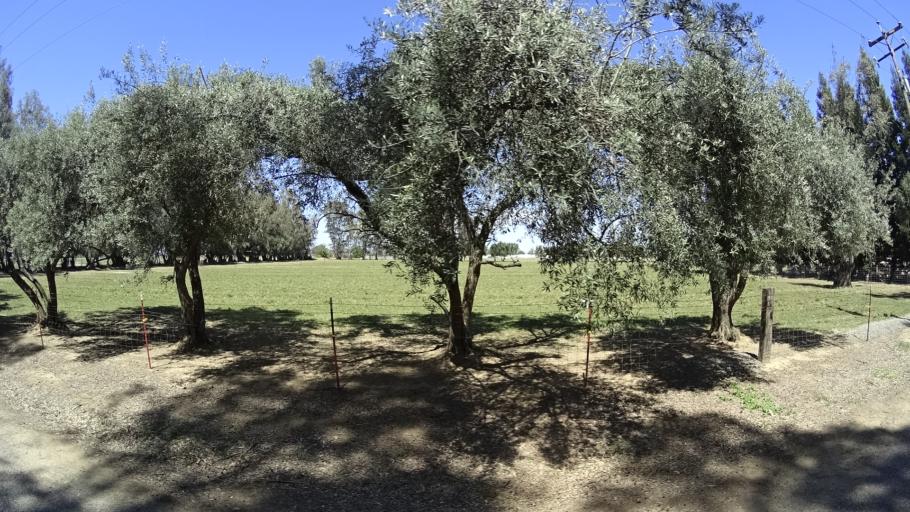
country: US
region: California
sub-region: Glenn County
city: Orland
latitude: 39.7330
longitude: -122.2007
